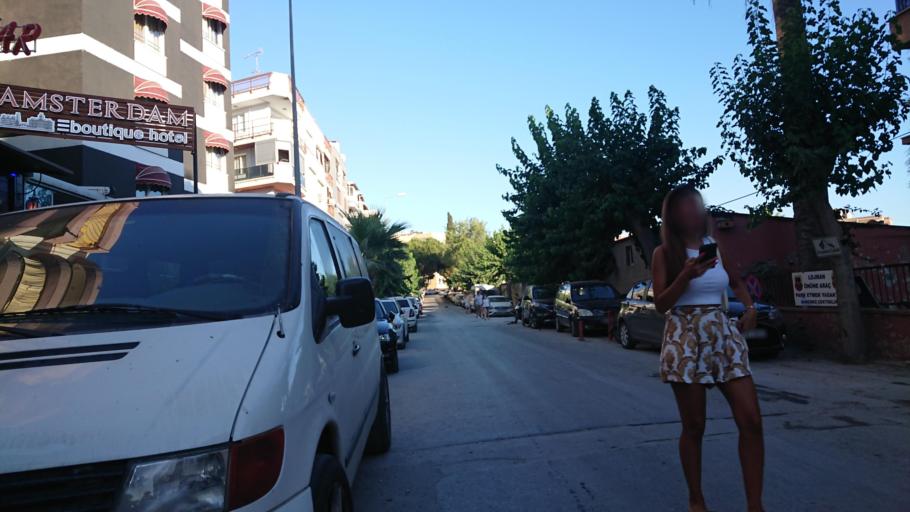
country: TR
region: Aydin
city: Kusadasi
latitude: 37.8647
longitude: 27.2635
